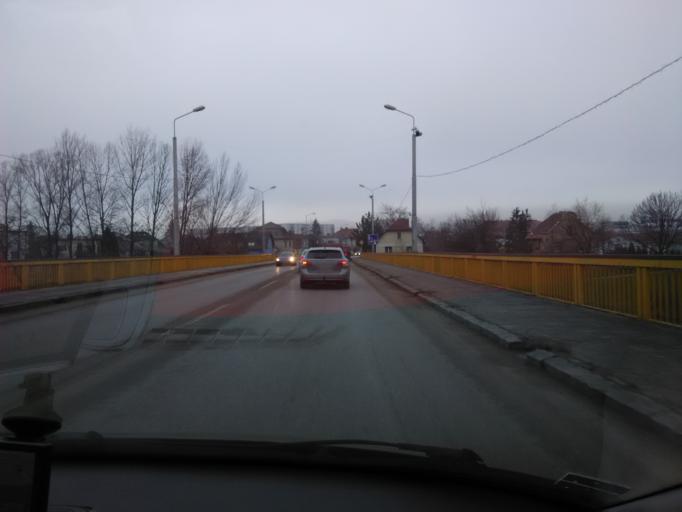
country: SK
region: Trenciansky
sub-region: Okres Trencin
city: Trencin
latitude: 48.8954
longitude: 18.0339
